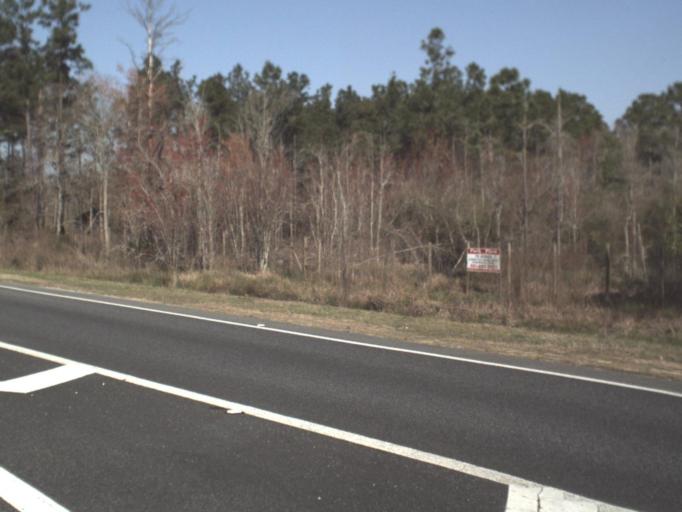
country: US
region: Florida
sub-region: Gadsden County
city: Midway
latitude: 30.4807
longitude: -84.3677
